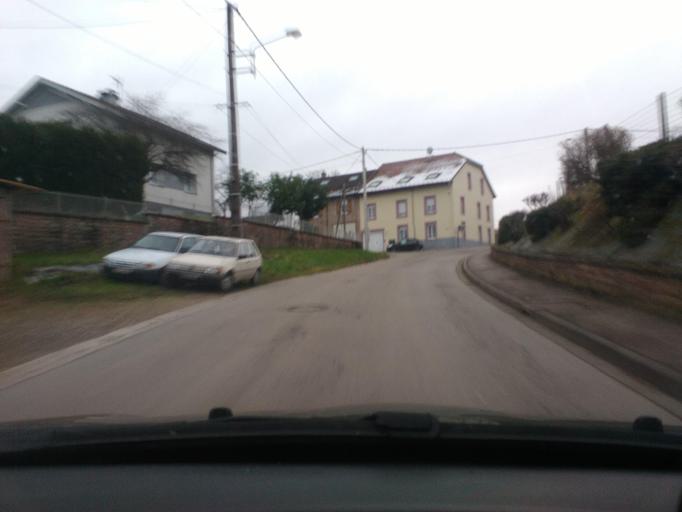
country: FR
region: Lorraine
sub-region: Departement des Vosges
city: Etival-Clairefontaine
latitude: 48.3618
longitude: 6.8654
